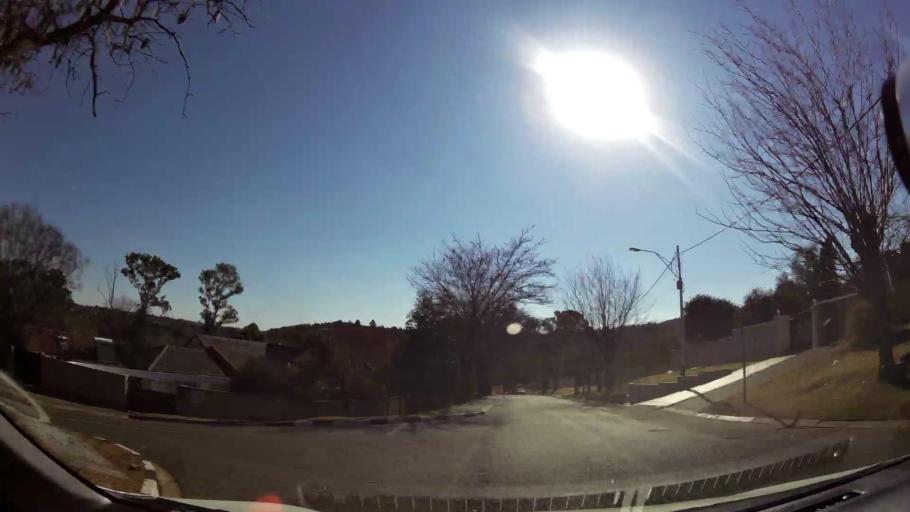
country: ZA
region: Gauteng
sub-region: City of Johannesburg Metropolitan Municipality
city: Johannesburg
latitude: -26.2726
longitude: 28.0111
